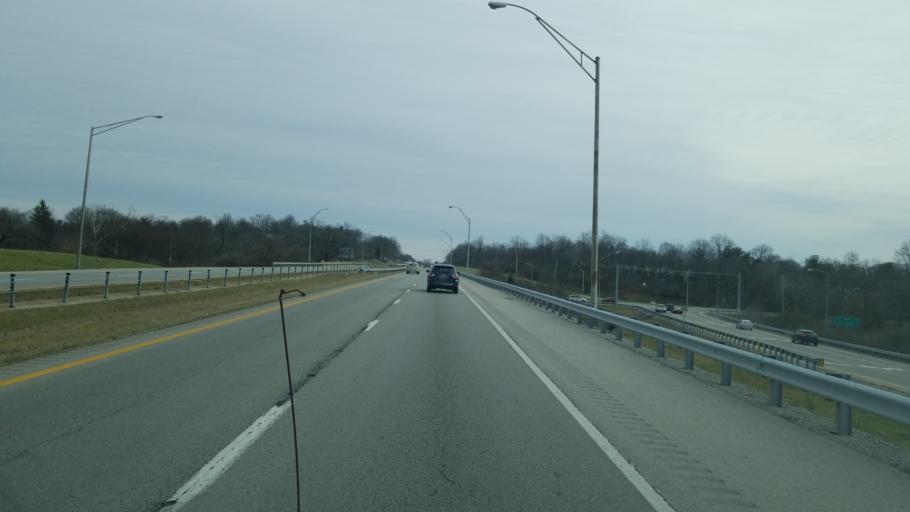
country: US
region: Kentucky
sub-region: Fayette County
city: Lexington
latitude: 37.9907
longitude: -84.4970
